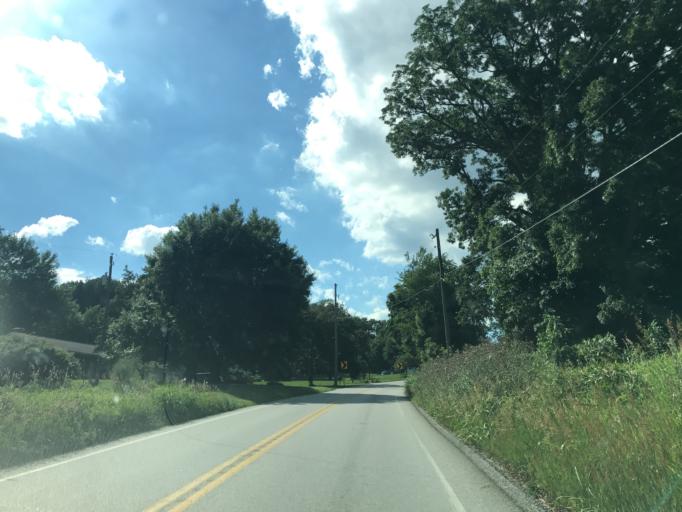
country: US
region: Pennsylvania
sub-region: York County
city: Glen Rock
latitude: 39.7439
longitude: -76.8010
